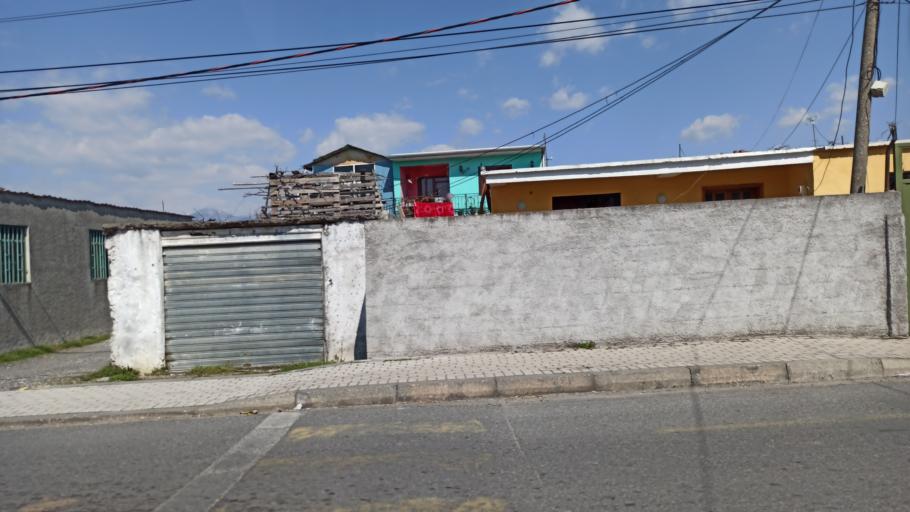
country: AL
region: Shkoder
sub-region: Rrethi i Shkodres
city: Shkoder
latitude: 42.0562
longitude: 19.5162
